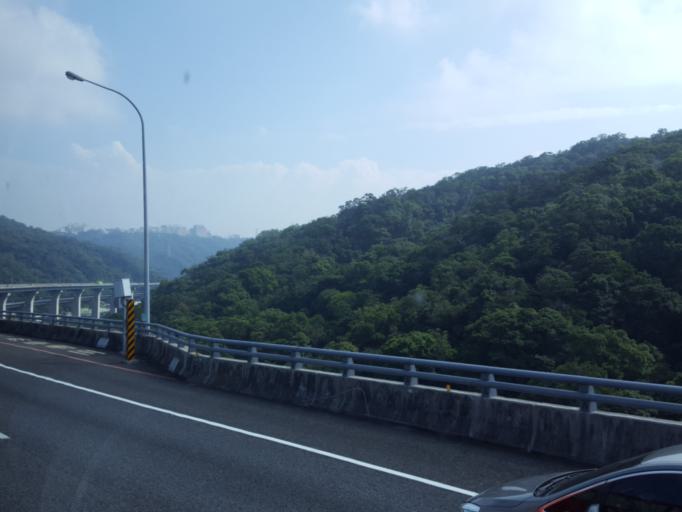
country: TW
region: Taipei
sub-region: Taipei
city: Banqiao
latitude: 25.0650
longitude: 121.3887
